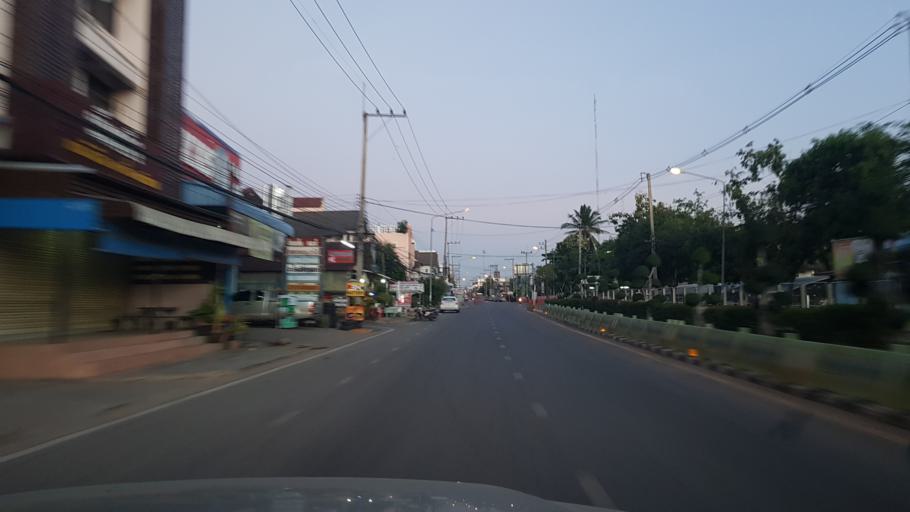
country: TH
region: Chaiyaphum
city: Phu Khiao
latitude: 16.3669
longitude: 102.1314
